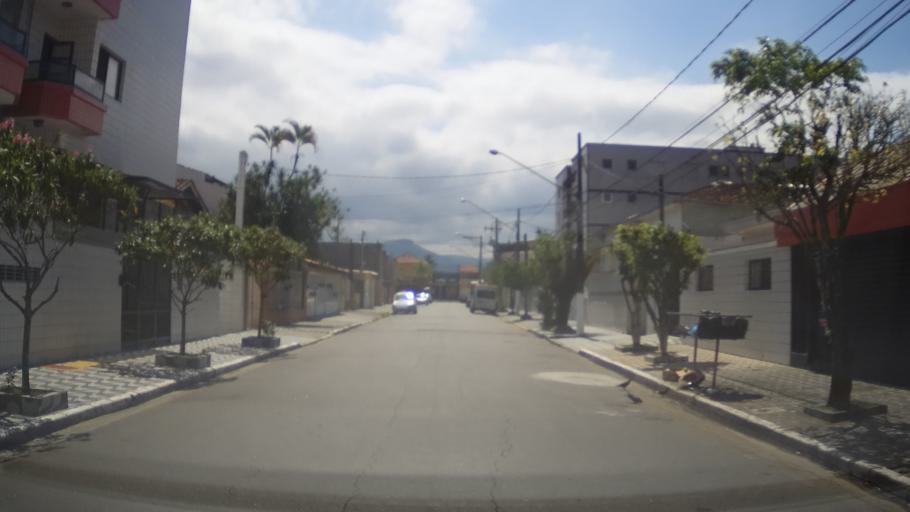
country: BR
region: Sao Paulo
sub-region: Praia Grande
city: Praia Grande
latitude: -24.0197
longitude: -46.4595
